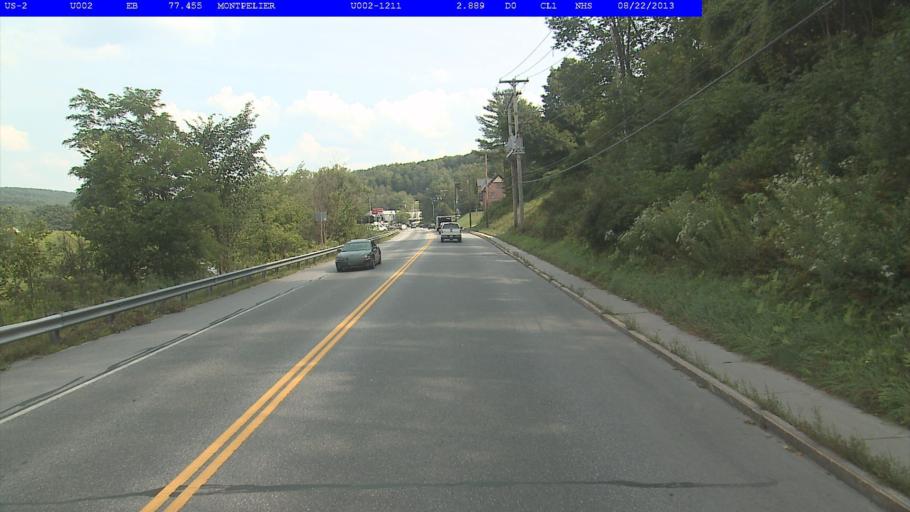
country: US
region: Vermont
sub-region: Washington County
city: Montpelier
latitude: 44.2500
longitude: -72.5681
